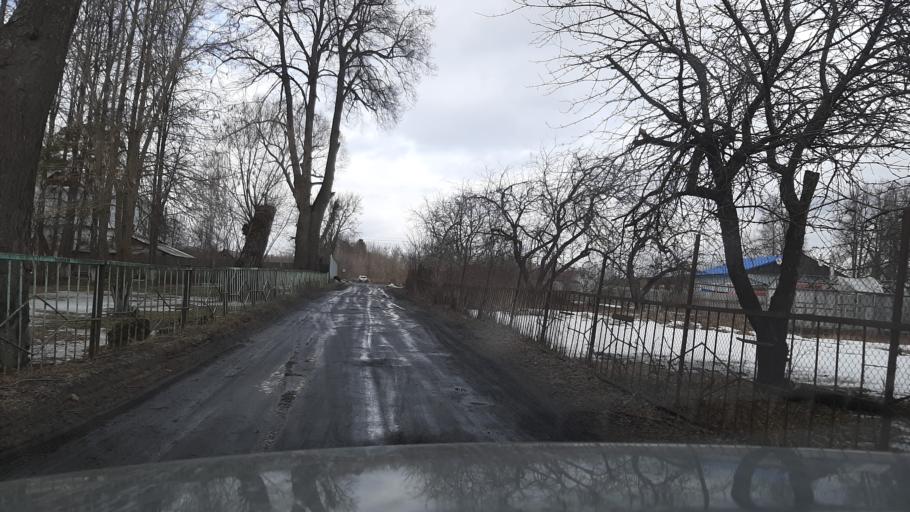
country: RU
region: Ivanovo
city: Teykovo
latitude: 56.8972
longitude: 40.6640
